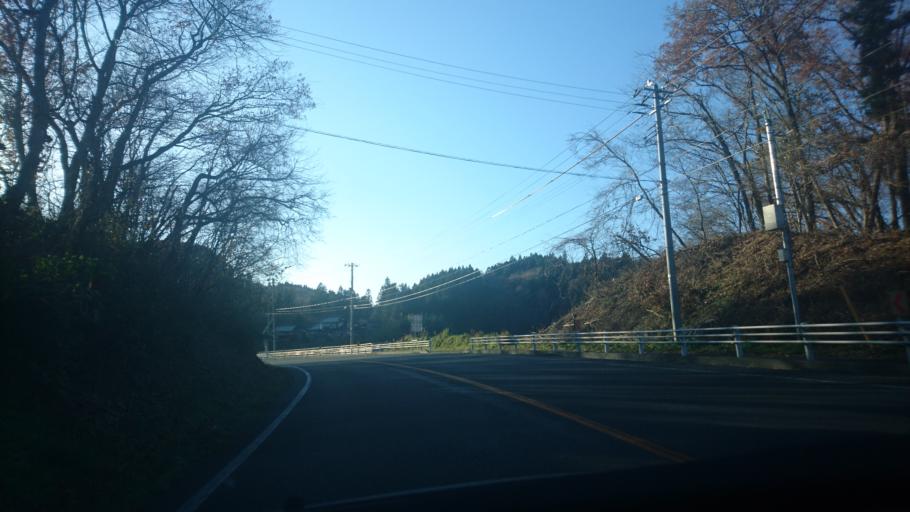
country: JP
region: Iwate
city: Ichinoseki
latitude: 38.9035
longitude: 141.2104
